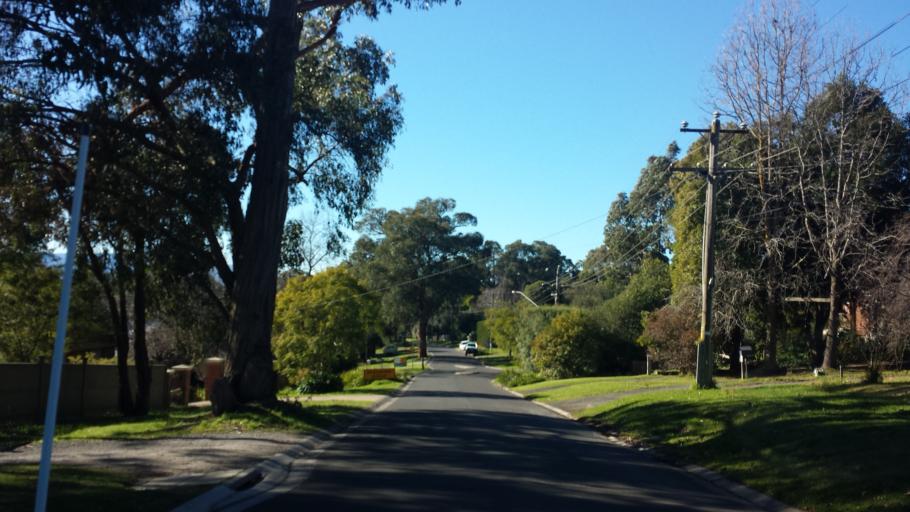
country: AU
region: Victoria
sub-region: Yarra Ranges
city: Mount Evelyn
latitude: -37.7777
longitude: 145.3910
